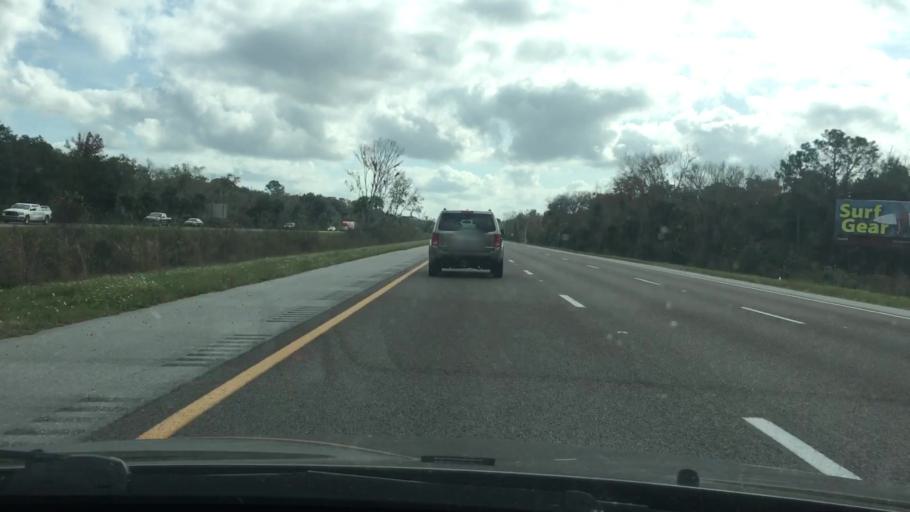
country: US
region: Florida
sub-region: Volusia County
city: Edgewater
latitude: 28.9435
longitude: -80.9475
